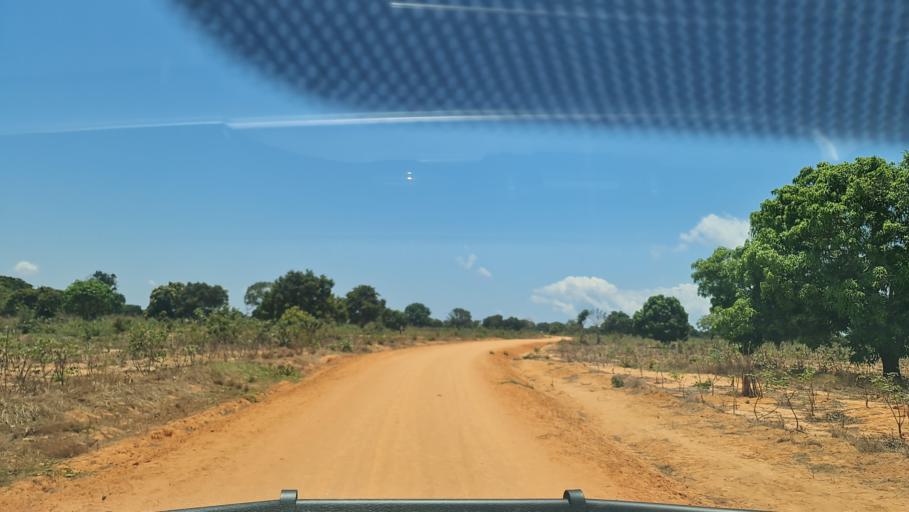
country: MZ
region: Nampula
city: Nacala
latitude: -14.2215
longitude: 40.6845
